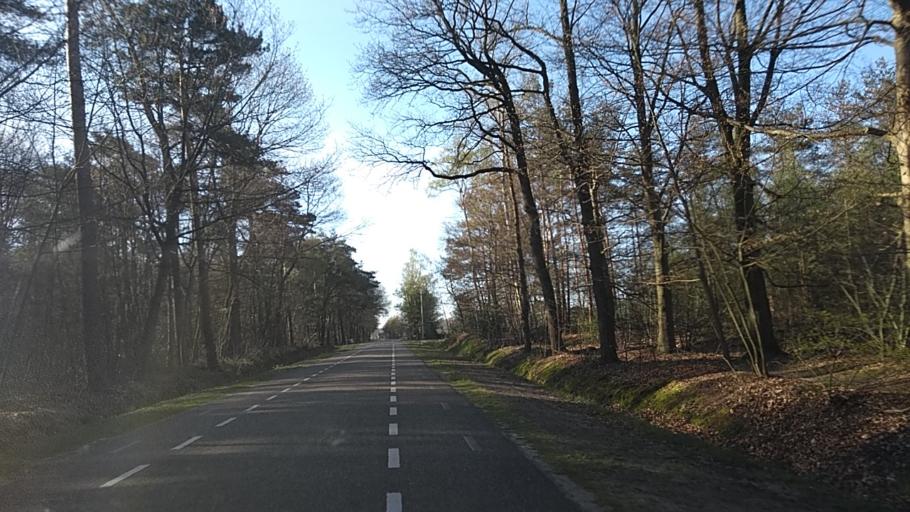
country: NL
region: Overijssel
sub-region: Gemeente Hof van Twente
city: Delden
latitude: 52.2697
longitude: 6.6705
